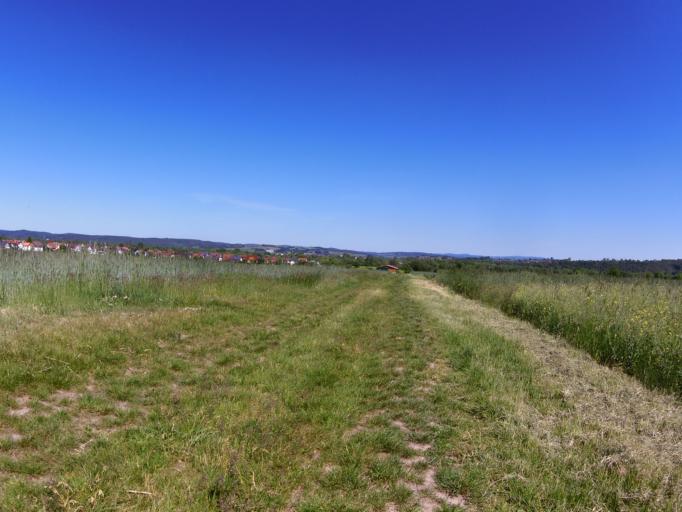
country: DE
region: Thuringia
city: Dankmarshausen
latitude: 50.9430
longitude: 10.0327
